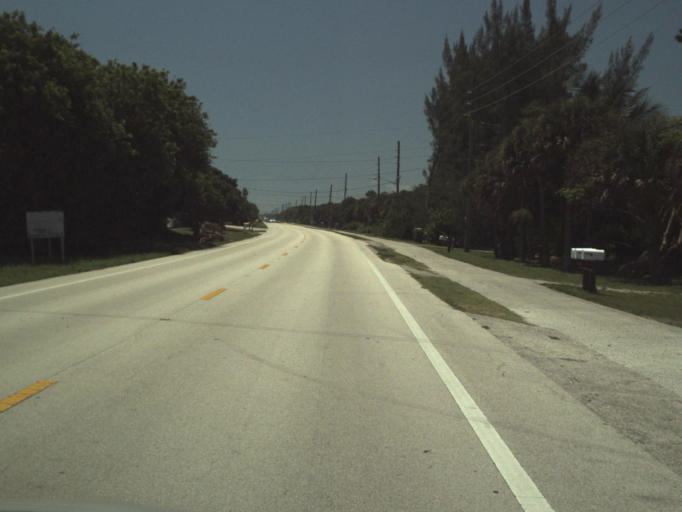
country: US
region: Florida
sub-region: Brevard County
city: Micco
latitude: 27.9109
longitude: -80.4766
